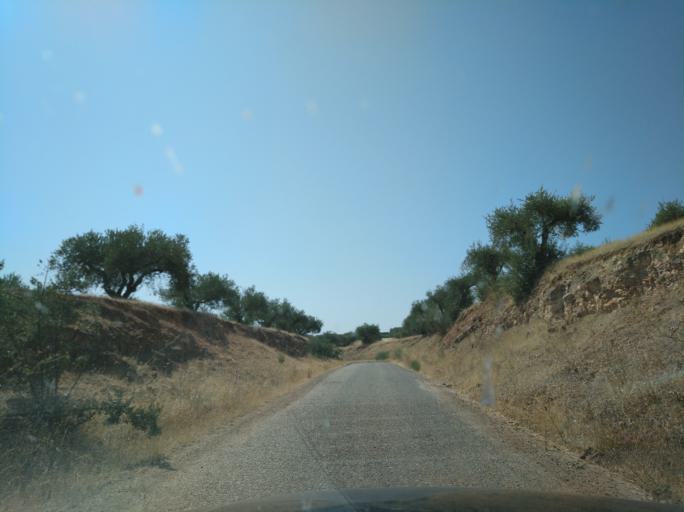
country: PT
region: Portalegre
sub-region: Campo Maior
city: Campo Maior
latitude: 39.0673
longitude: -7.0145
